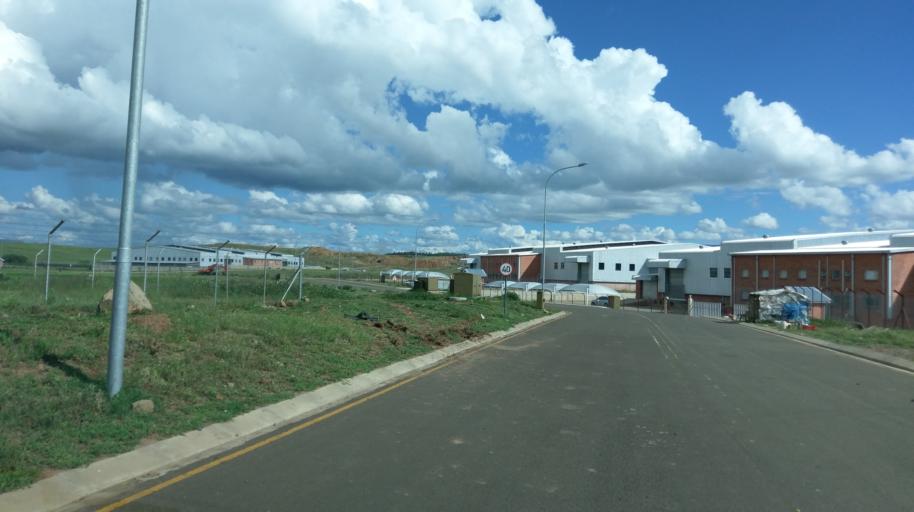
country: LS
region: Maseru
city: Maseru
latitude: -29.3815
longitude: 27.4843
